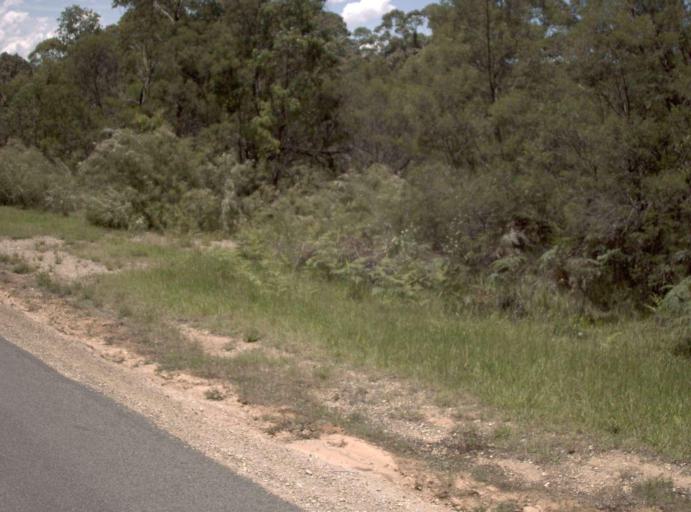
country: AU
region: New South Wales
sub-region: Bombala
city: Bombala
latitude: -37.5446
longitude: 148.9370
